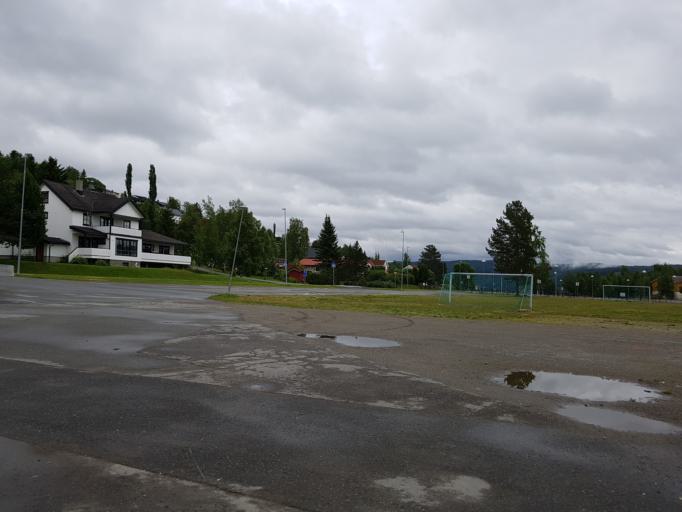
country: NO
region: Sor-Trondelag
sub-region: Selbu
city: Mebonden
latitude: 63.2270
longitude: 11.0328
